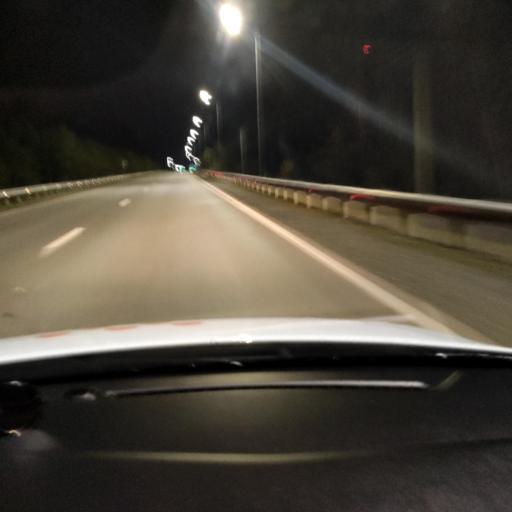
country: RU
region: Tatarstan
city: Stolbishchi
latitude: 55.6362
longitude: 49.1076
